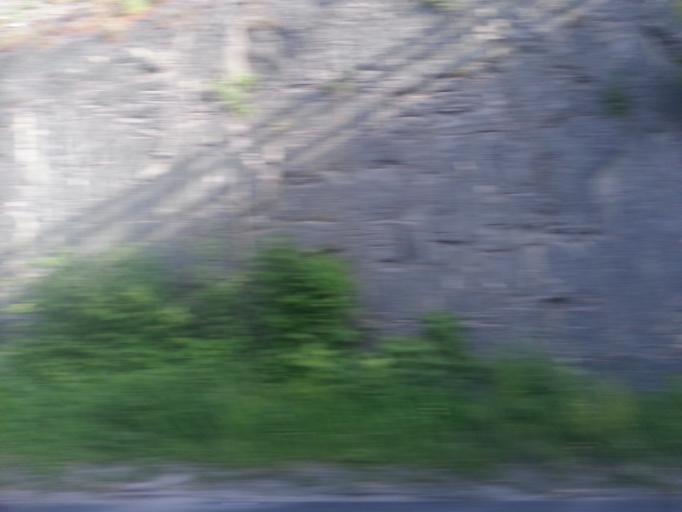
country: NO
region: Akershus
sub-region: Baerum
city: Sandvika
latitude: 59.8936
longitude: 10.5438
